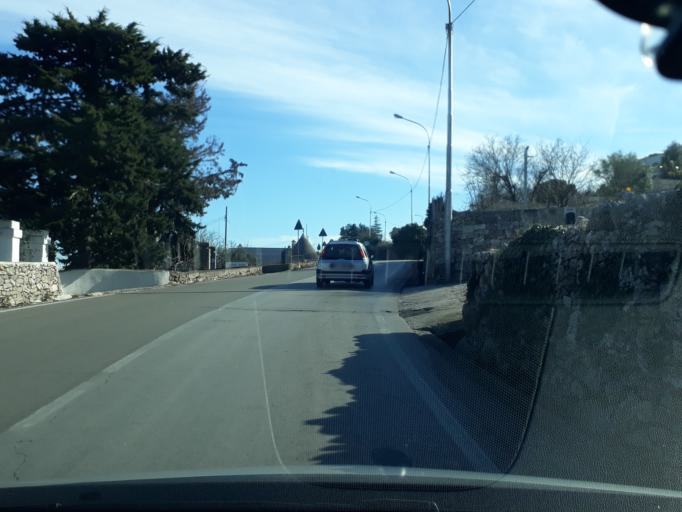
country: IT
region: Apulia
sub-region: Provincia di Taranto
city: Martina Franca
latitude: 40.7097
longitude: 17.3358
